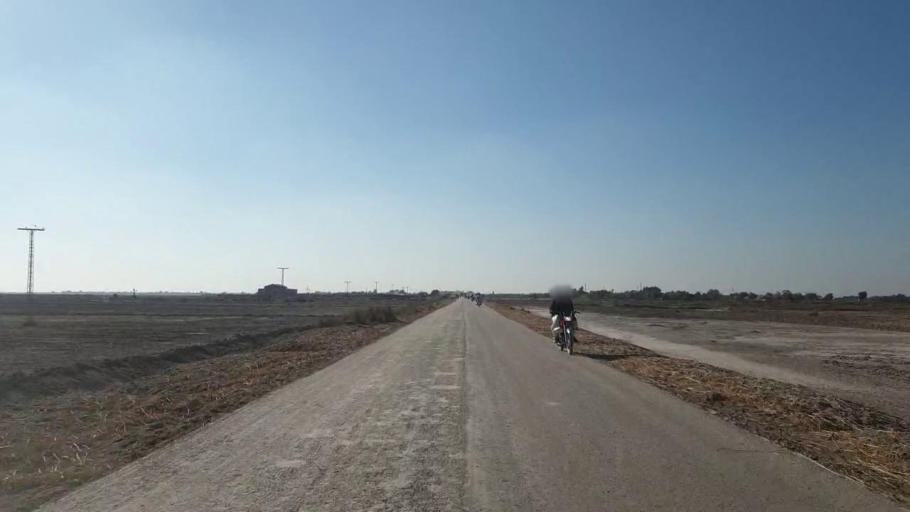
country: PK
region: Sindh
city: New Badah
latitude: 27.3250
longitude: 68.0475
